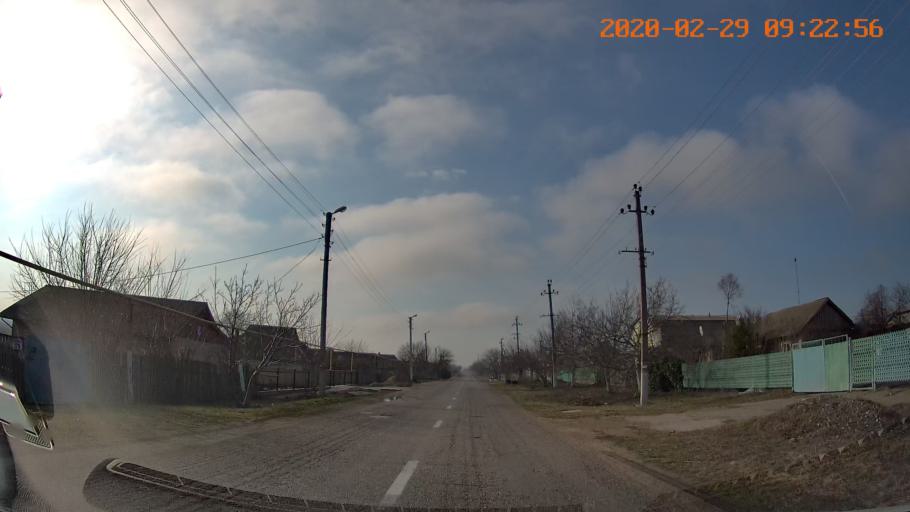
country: MD
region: Telenesti
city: Pervomaisc
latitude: 46.7308
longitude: 29.9627
